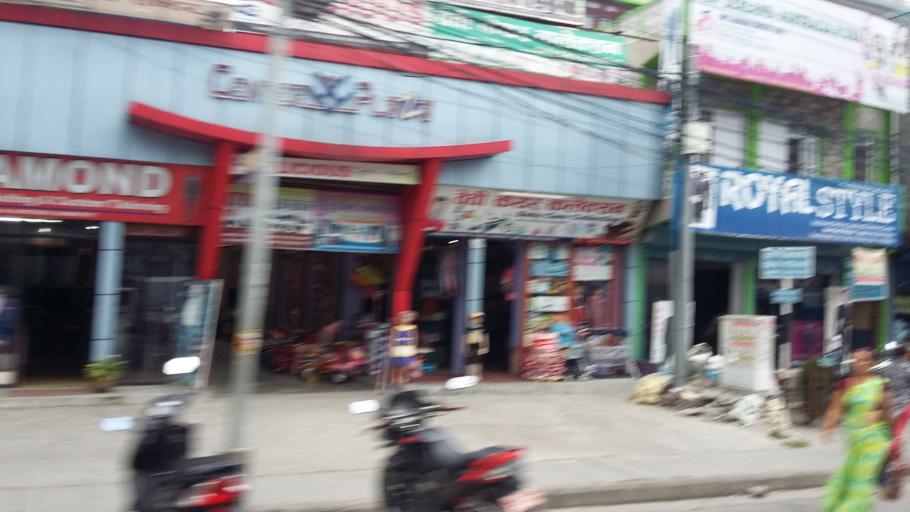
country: NP
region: Western Region
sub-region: Gandaki Zone
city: Pokhara
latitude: 28.2178
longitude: 83.9865
